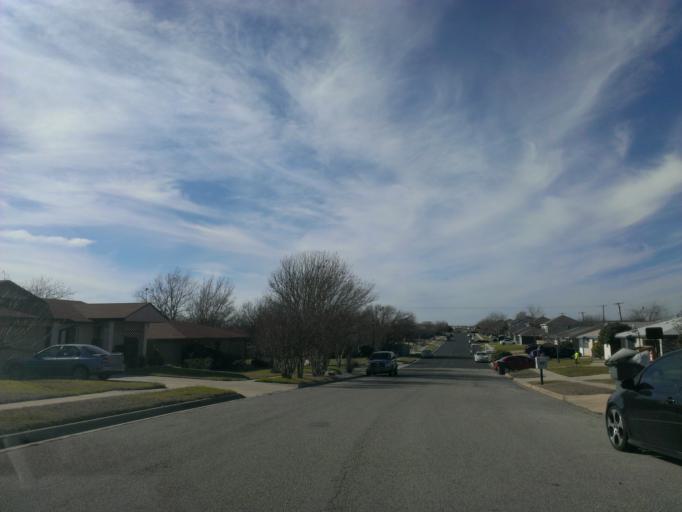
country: US
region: Texas
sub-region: Bell County
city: Killeen
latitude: 31.1382
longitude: -97.6902
